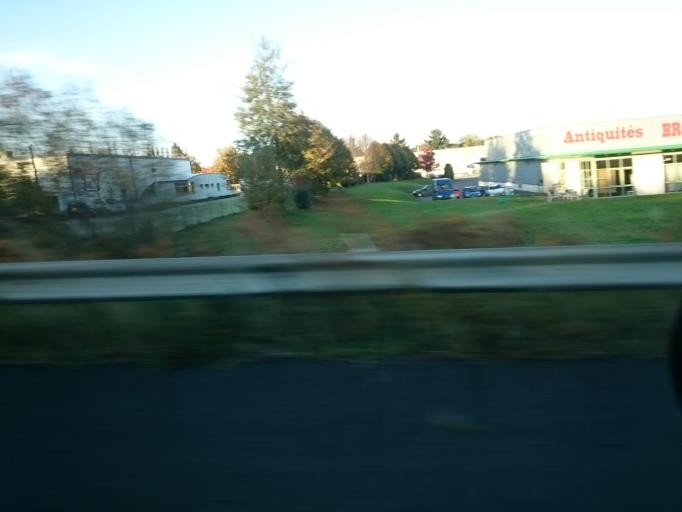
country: FR
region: Brittany
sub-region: Departement des Cotes-d'Armor
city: Plounevez-Moedec
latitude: 48.5587
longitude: -3.4899
